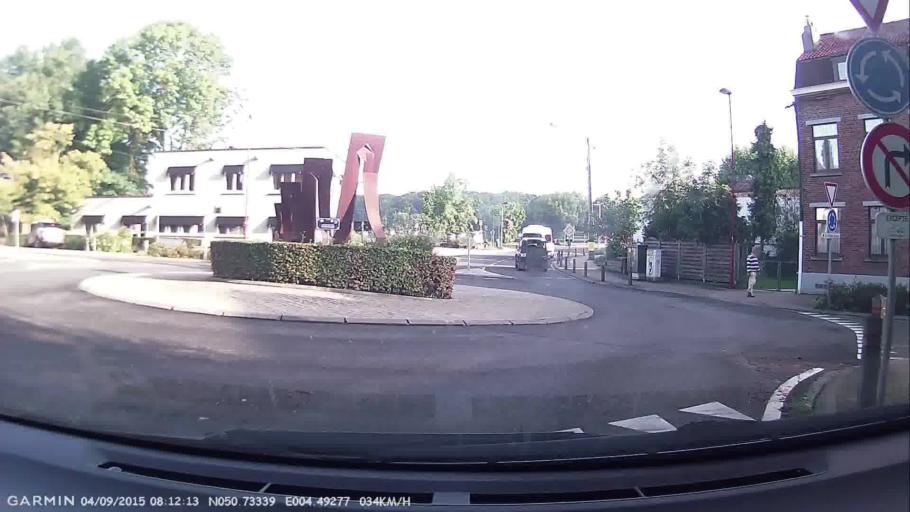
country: BE
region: Wallonia
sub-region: Province du Brabant Wallon
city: La Hulpe
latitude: 50.7335
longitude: 4.4927
